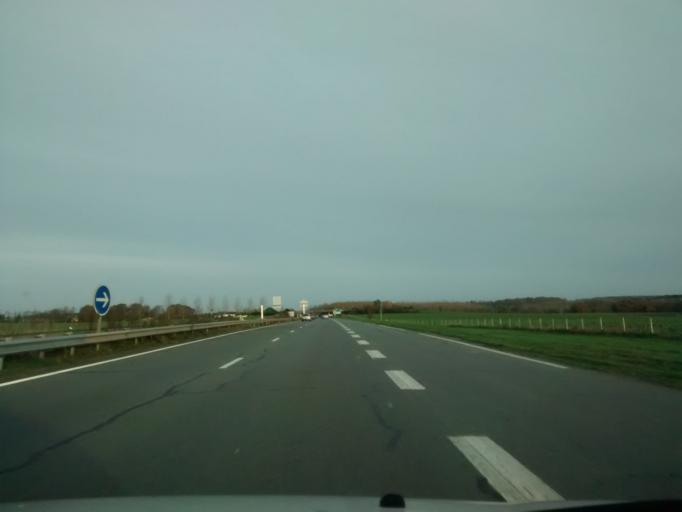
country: FR
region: Brittany
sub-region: Departement d'Ille-et-Vilaine
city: Saint-Pere
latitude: 48.5488
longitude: -1.9241
